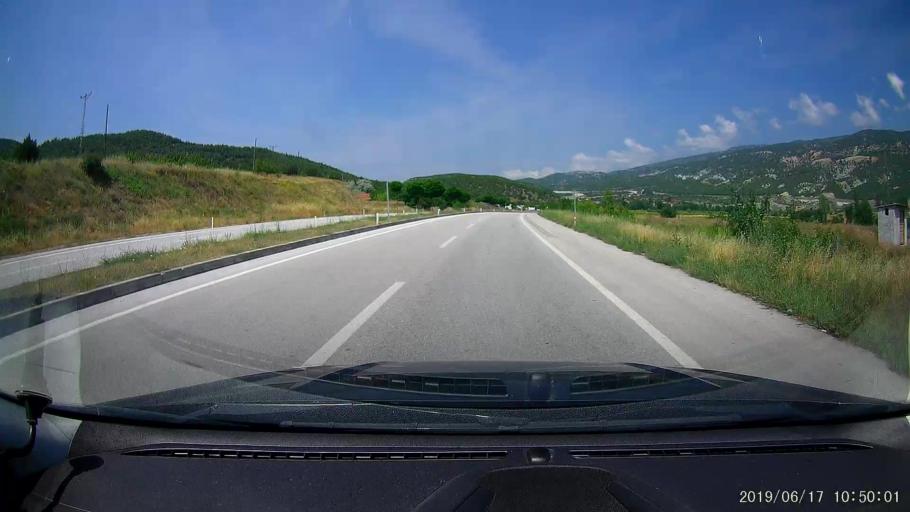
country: TR
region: Corum
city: Hacihamza
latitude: 41.0975
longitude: 34.3956
